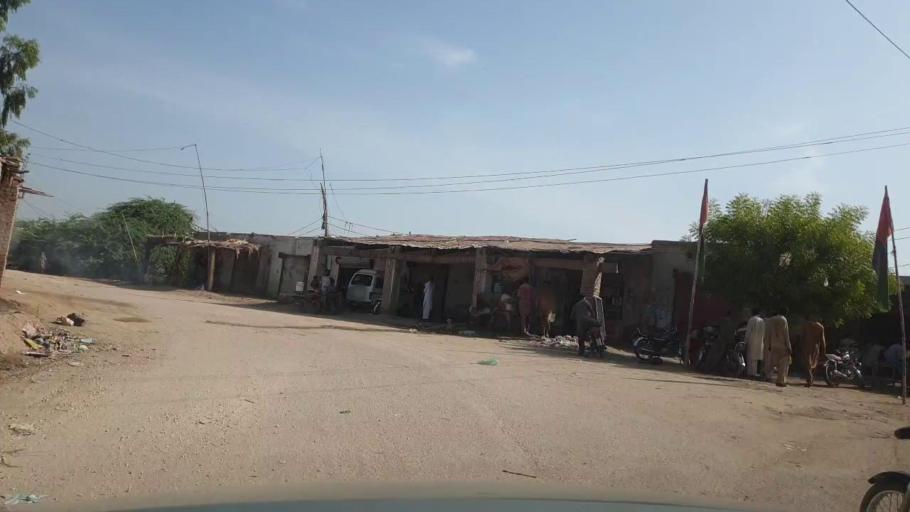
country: PK
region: Sindh
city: Rohri
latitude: 27.6765
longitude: 68.8816
